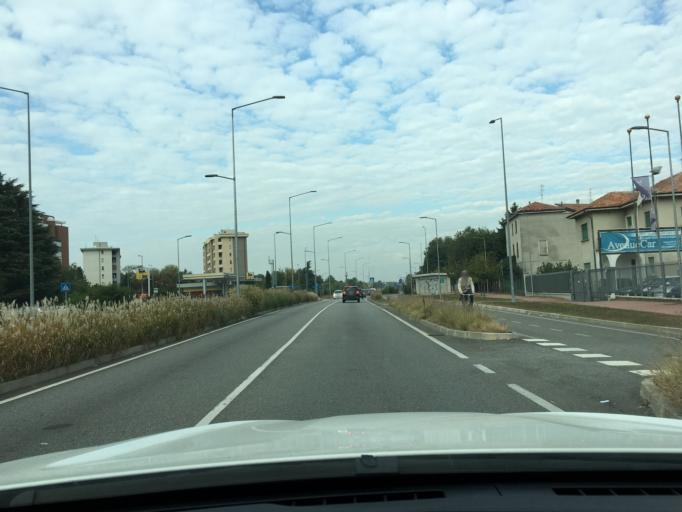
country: IT
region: Lombardy
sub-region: Provincia di Monza e Brianza
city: Muggio
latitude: 45.5734
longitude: 9.2470
